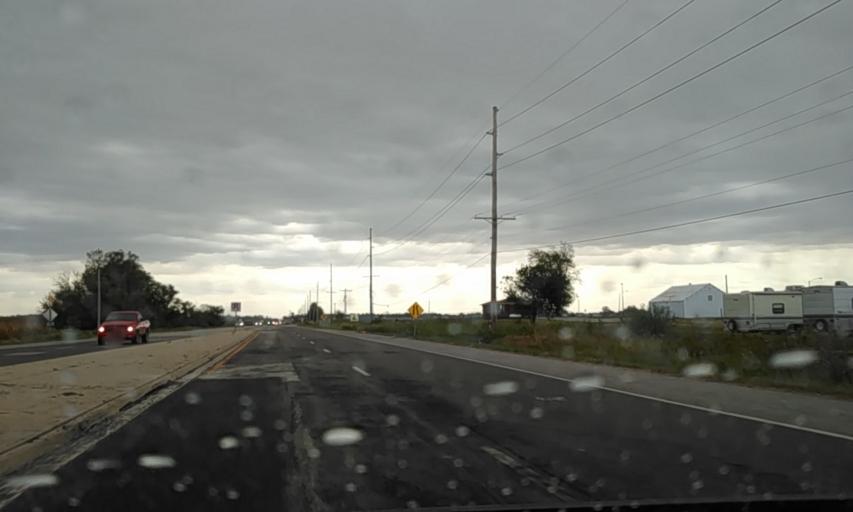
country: US
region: Illinois
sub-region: Madison County
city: Troy
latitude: 38.7174
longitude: -89.9082
